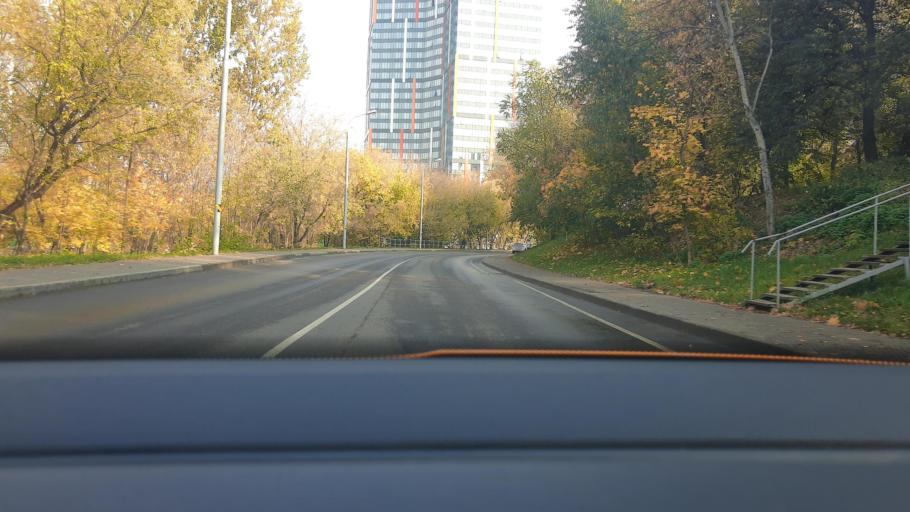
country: RU
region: Moskovskaya
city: Kastanayevo
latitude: 55.7098
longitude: 37.5013
